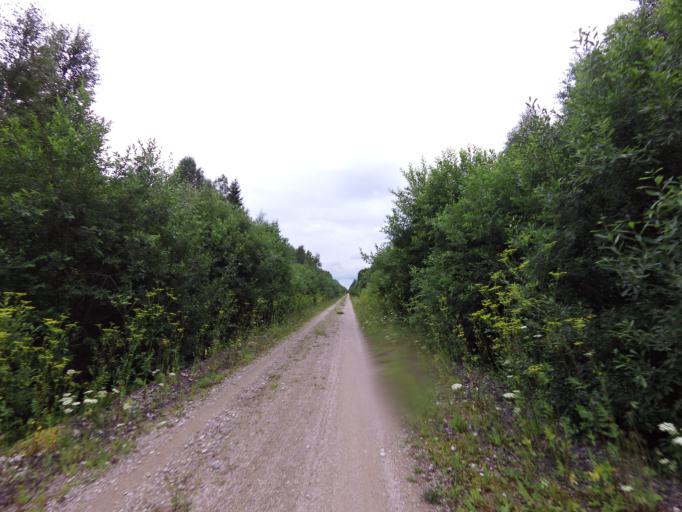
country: EE
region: Harju
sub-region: Nissi vald
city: Turba
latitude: 59.0109
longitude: 24.0805
